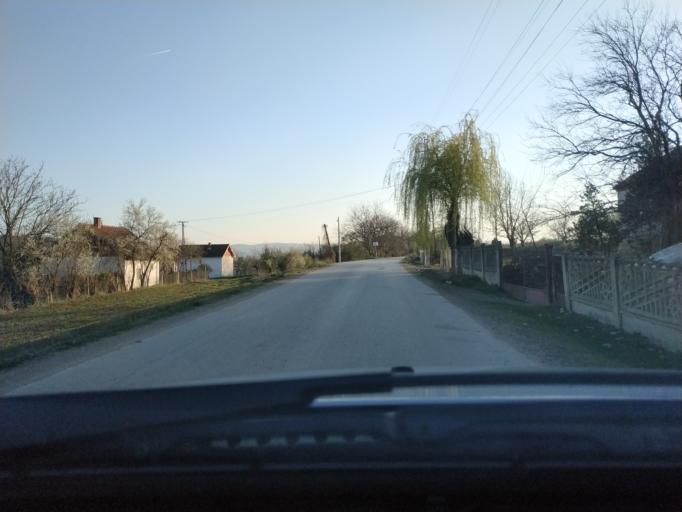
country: RS
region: Central Serbia
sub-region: Nisavski Okrug
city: Aleksinac
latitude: 43.5042
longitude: 21.7938
